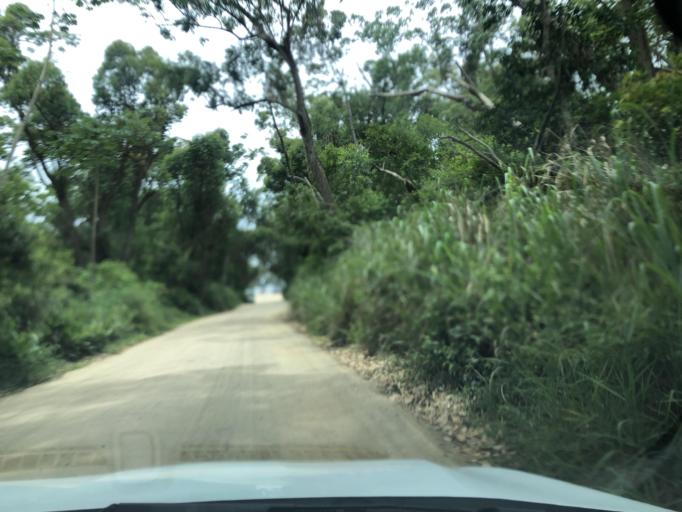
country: BR
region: Santa Catarina
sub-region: Florianopolis
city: Lagoa
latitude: -27.5234
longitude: -48.4198
